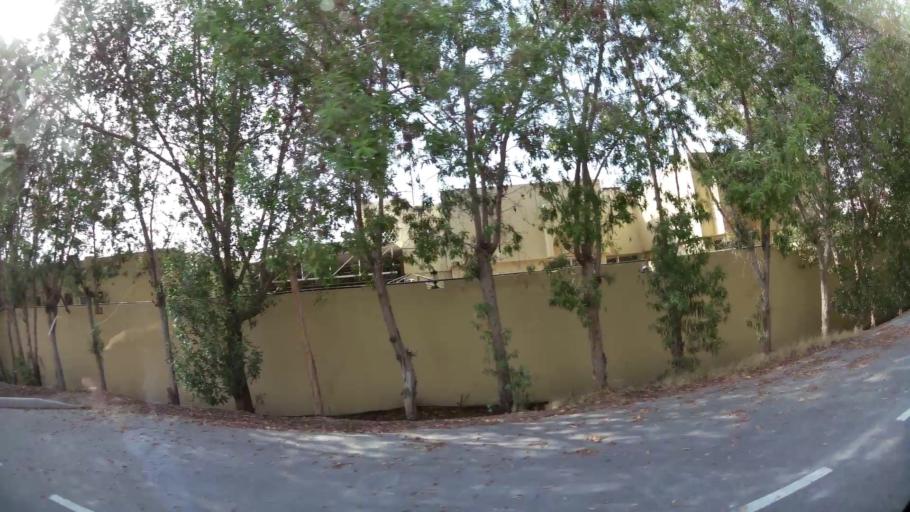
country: AE
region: Ash Shariqah
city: Sharjah
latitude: 25.2475
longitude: 55.4213
